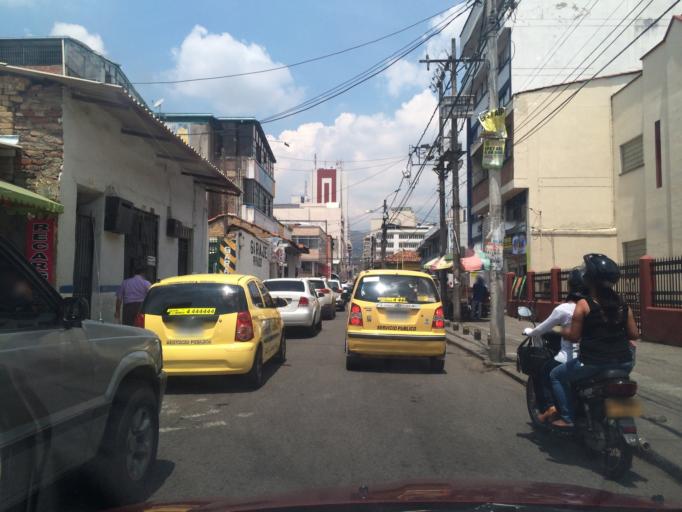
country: CO
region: Valle del Cauca
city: Cali
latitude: 3.4543
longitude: -76.5284
